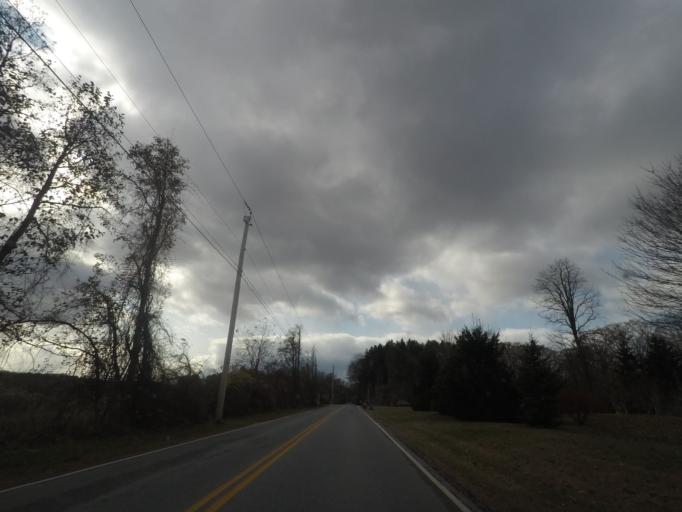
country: US
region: New York
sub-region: Saratoga County
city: Ballston Spa
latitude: 43.0128
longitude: -73.8042
